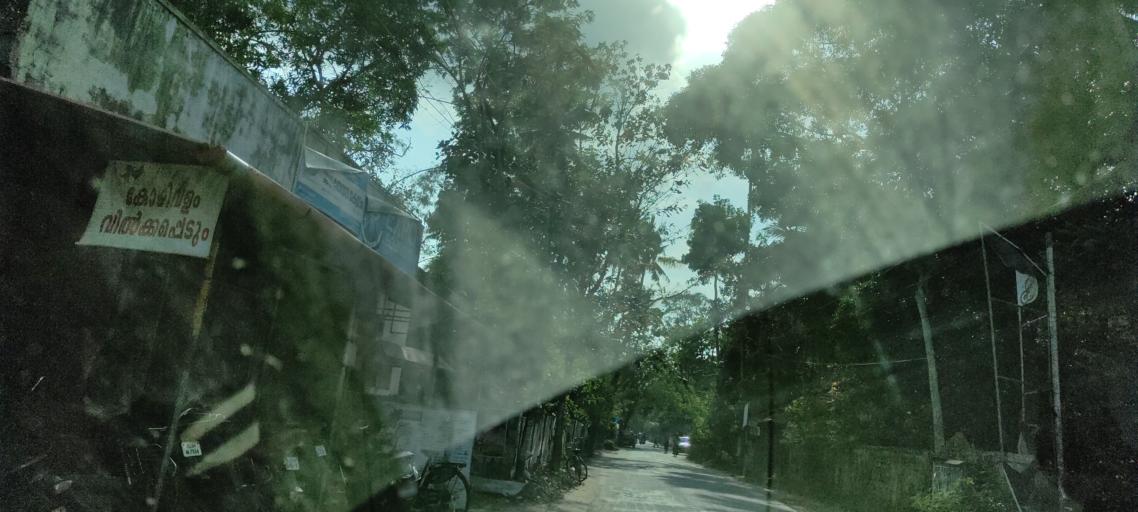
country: IN
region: Kerala
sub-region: Alappuzha
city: Vayalar
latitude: 9.6877
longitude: 76.3173
